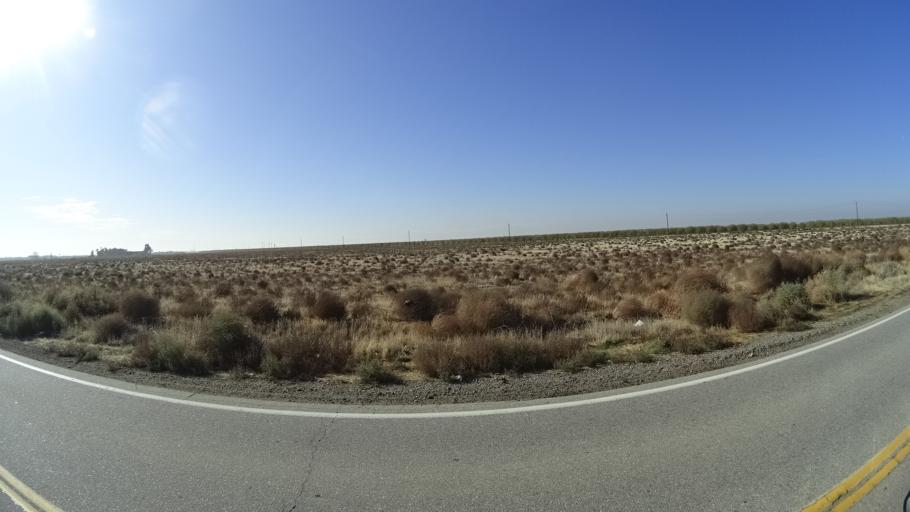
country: US
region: California
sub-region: Kern County
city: Rosedale
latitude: 35.4328
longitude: -119.1516
